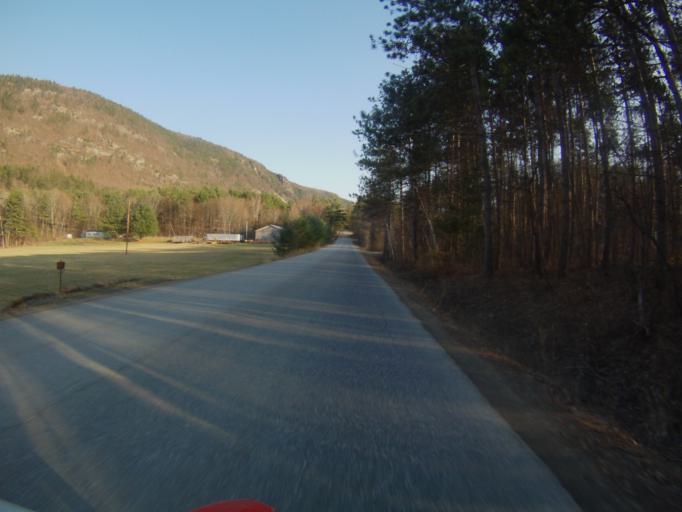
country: US
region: Vermont
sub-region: Addison County
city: Bristol
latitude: 44.1187
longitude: -73.0802
